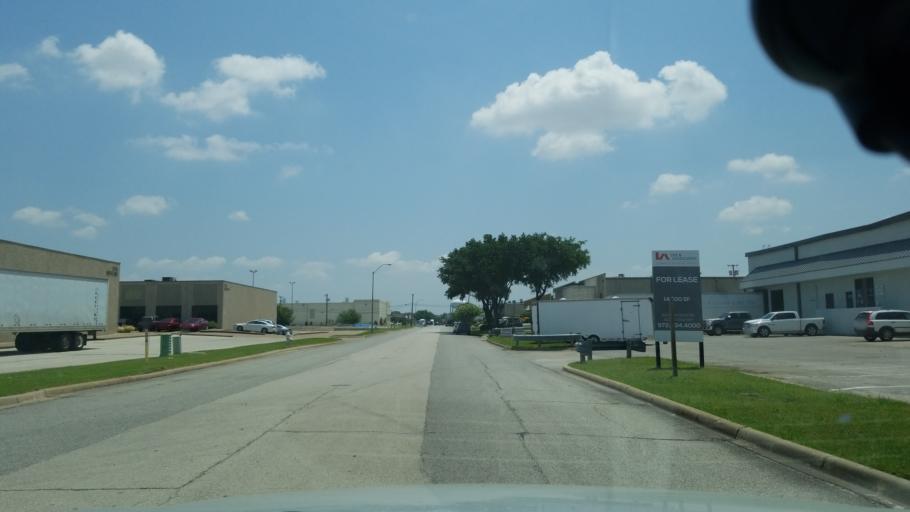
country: US
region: Texas
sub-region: Dallas County
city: Carrollton
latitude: 32.9515
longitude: -96.8695
